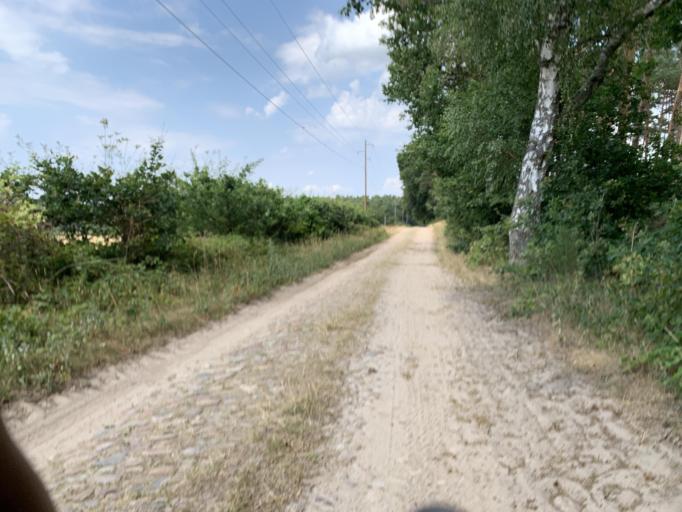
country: DE
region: Lower Saxony
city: Thomasburg
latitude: 53.2022
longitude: 10.6361
